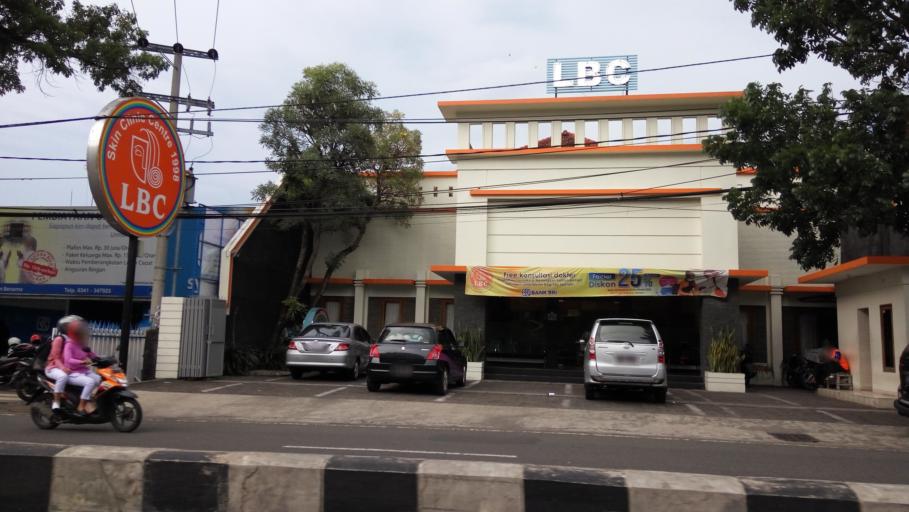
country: ID
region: East Java
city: Malang
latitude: -7.9777
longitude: 112.6222
